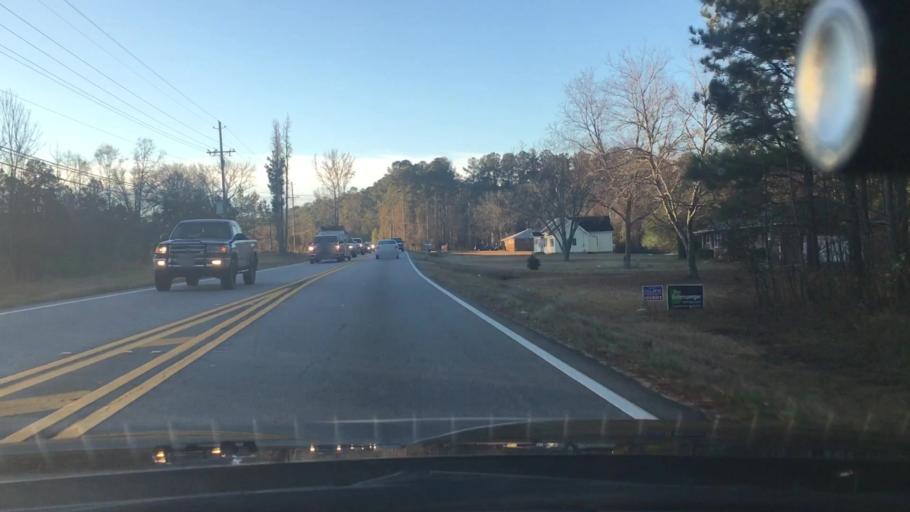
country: US
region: Georgia
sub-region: Fayette County
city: Peachtree City
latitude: 33.4054
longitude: -84.6821
